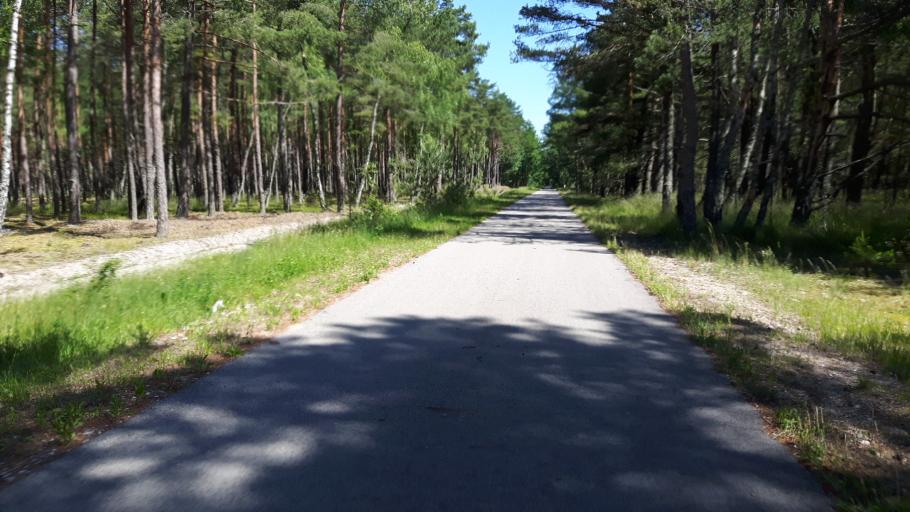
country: LT
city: Neringa
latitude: 55.3478
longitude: 21.0441
